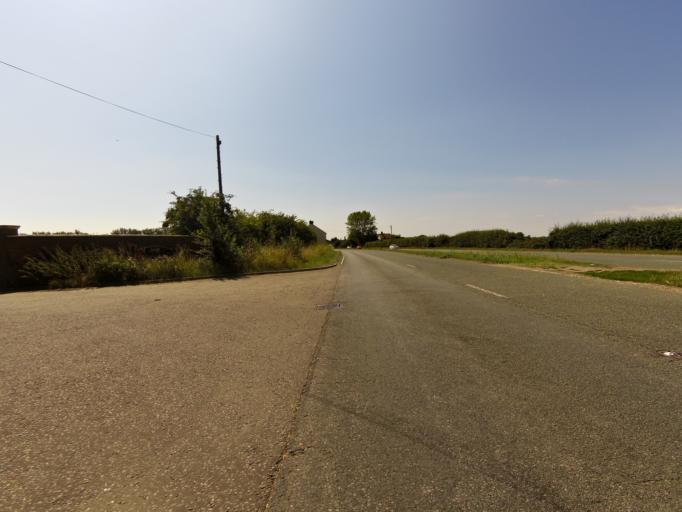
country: GB
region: England
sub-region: Suffolk
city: Capel Saint Mary
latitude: 52.0260
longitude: 1.0783
